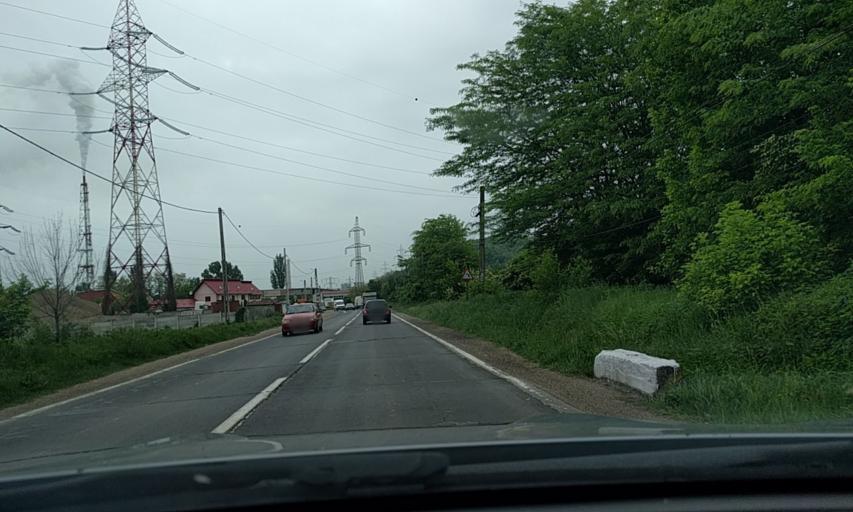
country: RO
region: Dambovita
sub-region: Comuna Aninoasa
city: Sateni
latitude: 44.9833
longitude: 25.4193
